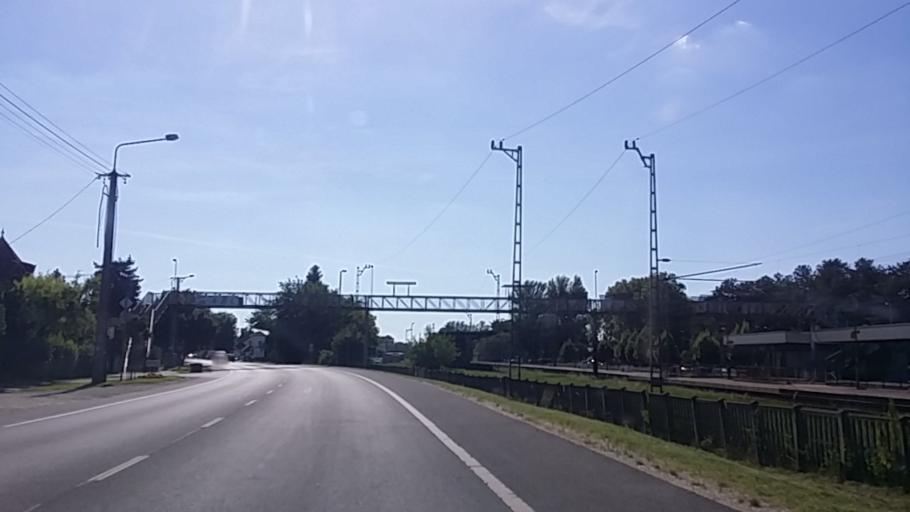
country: HU
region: Somogy
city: Balatonfenyves
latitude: 46.7135
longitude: 17.4840
